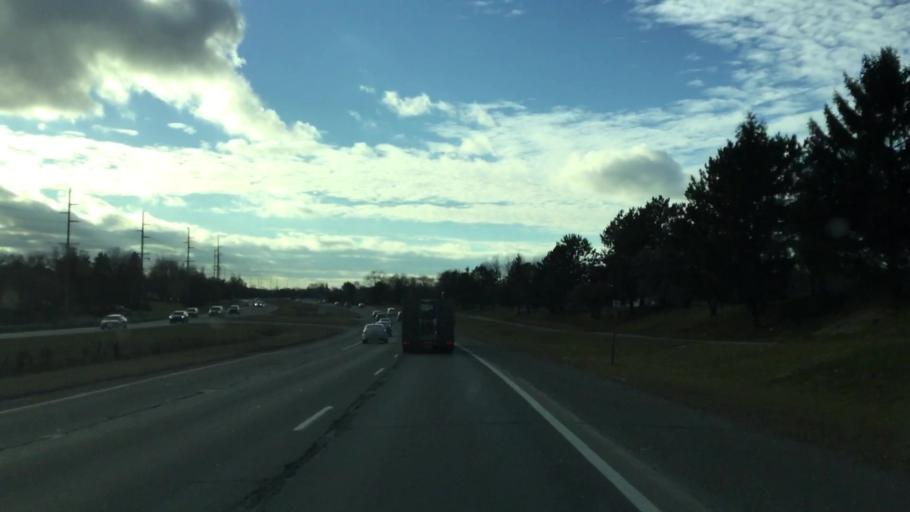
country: US
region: Michigan
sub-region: Oakland County
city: Milford
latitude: 42.6412
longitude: -83.6276
